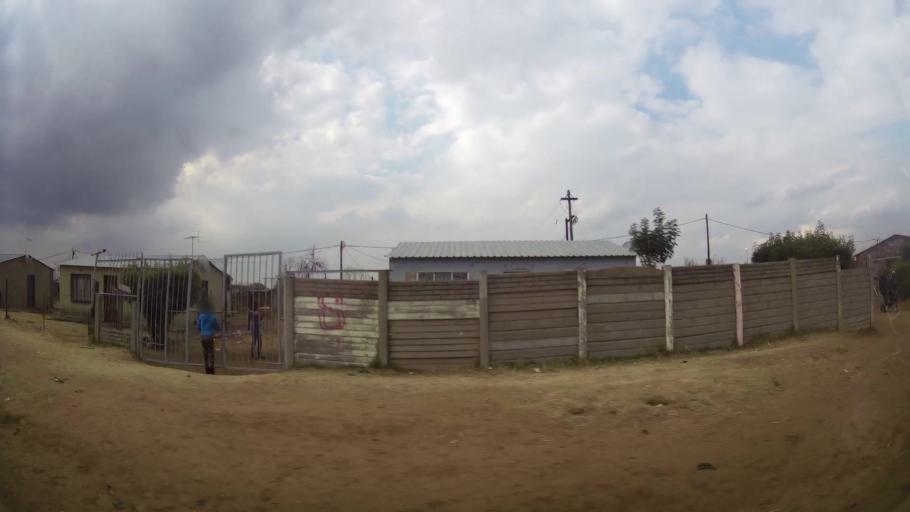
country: ZA
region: Orange Free State
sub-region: Fezile Dabi District Municipality
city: Sasolburg
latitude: -26.8643
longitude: 27.8659
